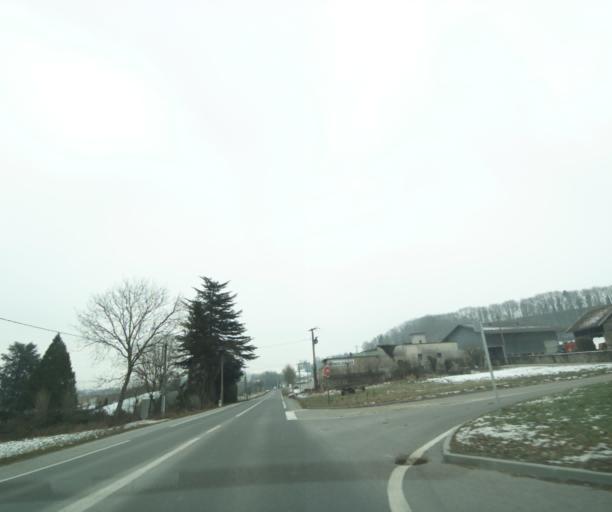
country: FR
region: Rhone-Alpes
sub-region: Departement de la Haute-Savoie
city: Arthaz-Pont-Notre-Dame
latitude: 46.1521
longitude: 6.2525
